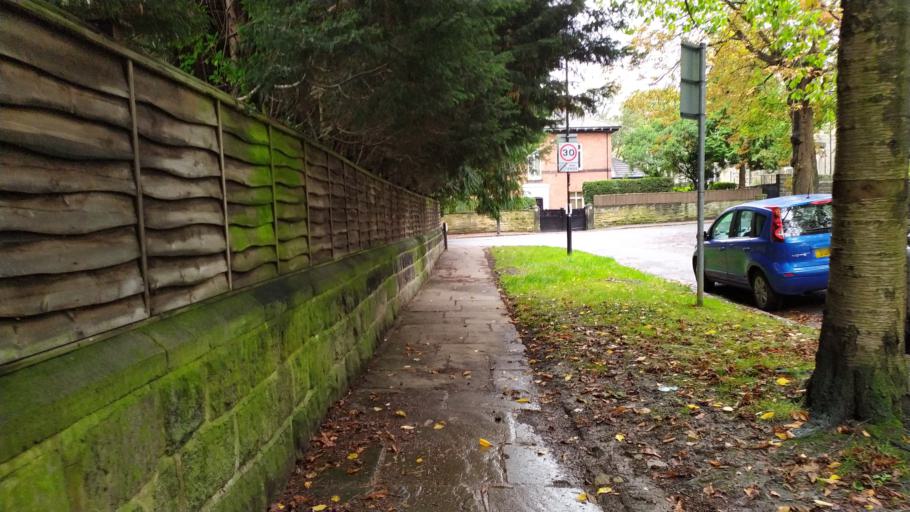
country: GB
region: England
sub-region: City and Borough of Leeds
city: Chapel Allerton
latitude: 53.8250
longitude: -1.5782
